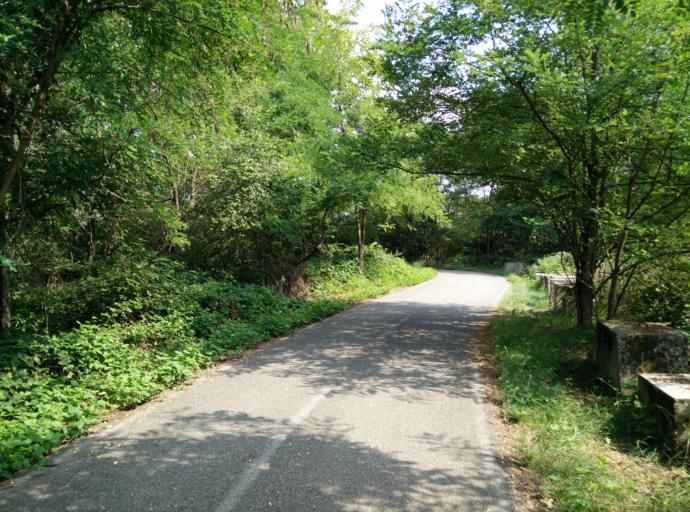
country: IT
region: Piedmont
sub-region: Provincia di Torino
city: Pasta
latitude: 45.0168
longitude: 7.5613
